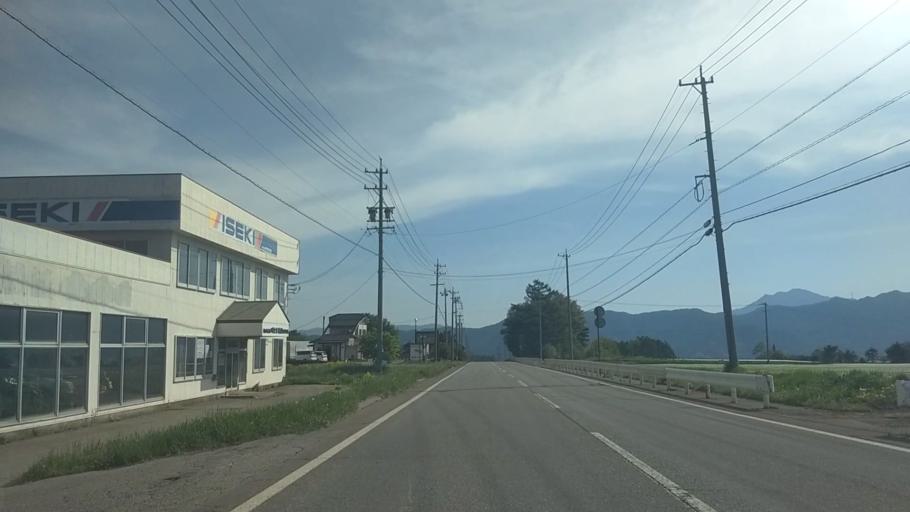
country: JP
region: Nagano
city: Saku
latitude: 35.9900
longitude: 138.4894
